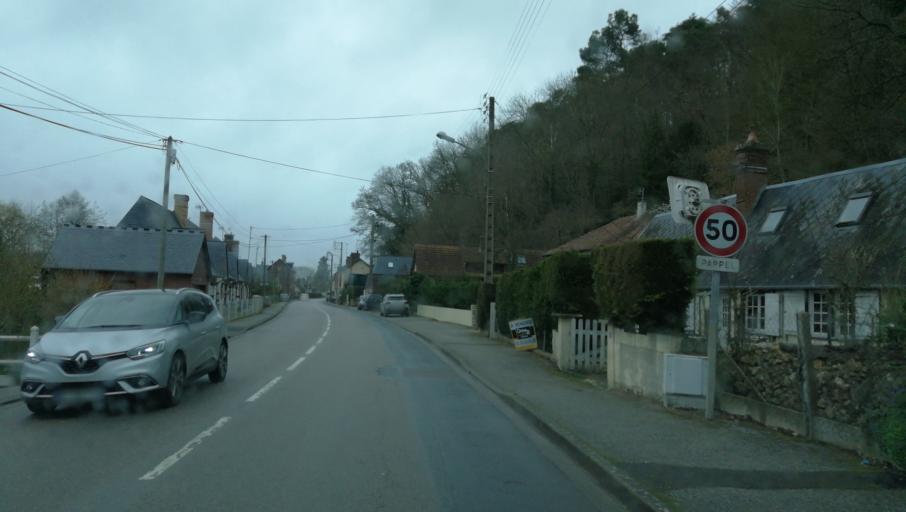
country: FR
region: Haute-Normandie
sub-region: Departement de l'Eure
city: Brionne
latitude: 49.1871
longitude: 0.7243
